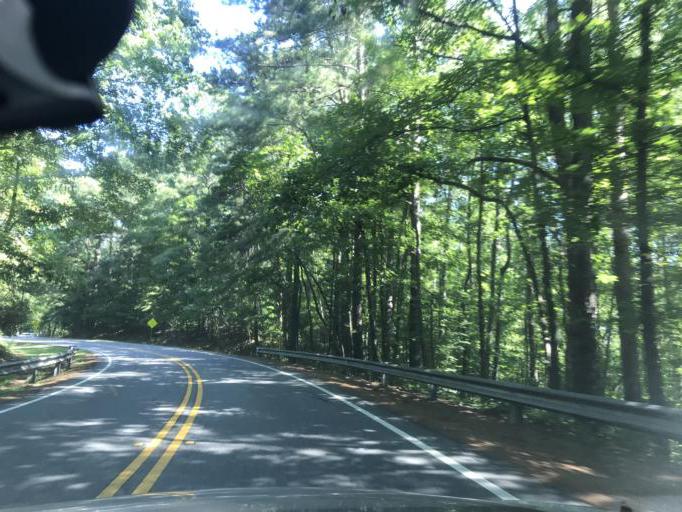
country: US
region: Georgia
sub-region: Gwinnett County
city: Sugar Hill
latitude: 34.1575
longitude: -84.0692
